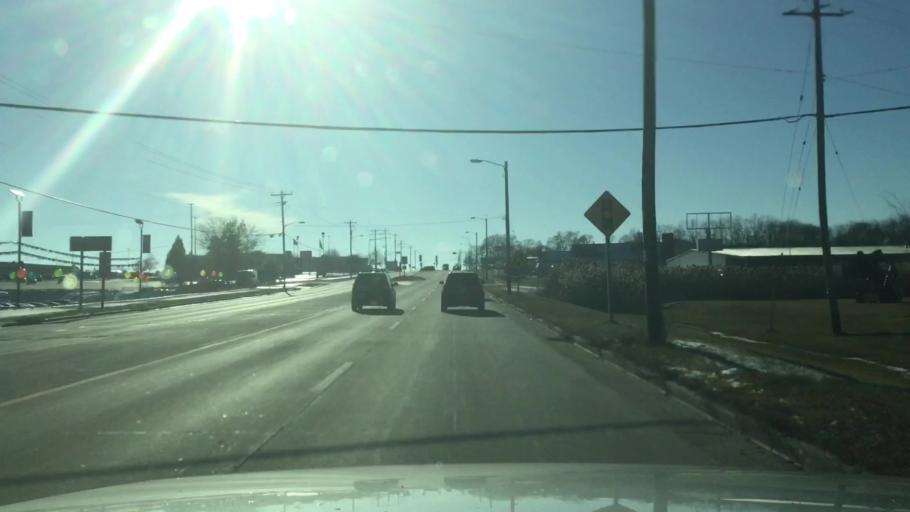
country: US
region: Wisconsin
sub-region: Racine County
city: Burlington
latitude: 42.6944
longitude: -88.2632
